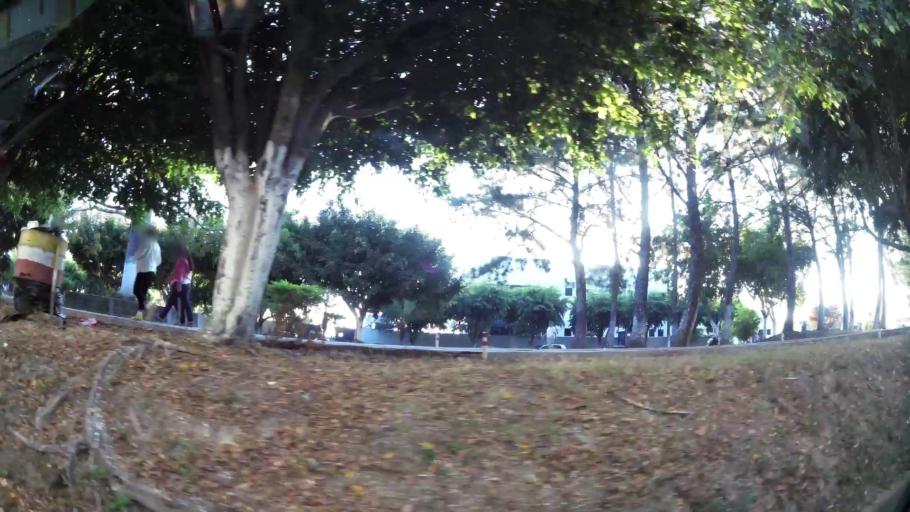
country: SV
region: La Libertad
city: Santa Tecla
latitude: 13.6793
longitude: -89.2636
